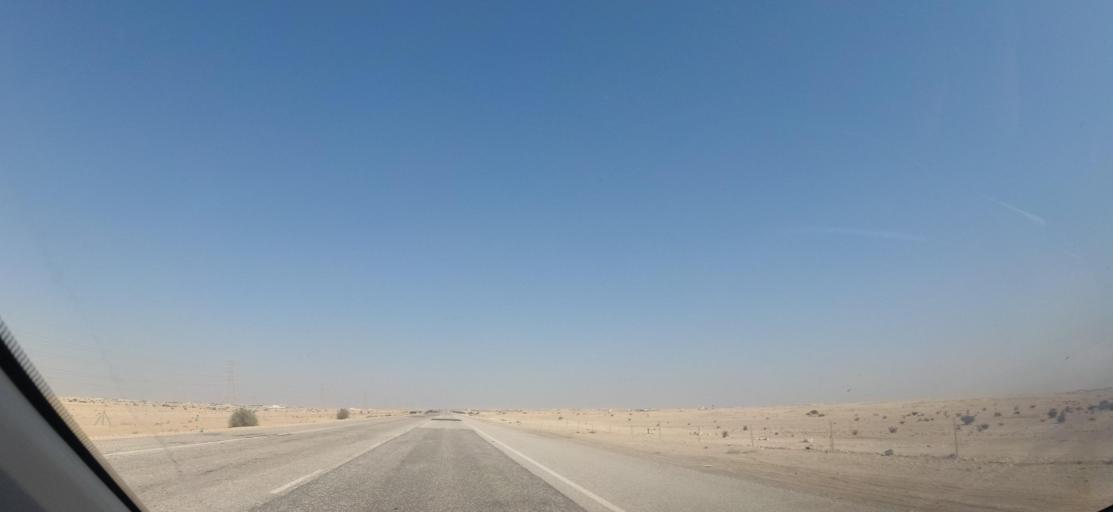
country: QA
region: Baladiyat ar Rayyan
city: Dukhan
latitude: 25.4773
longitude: 50.9490
